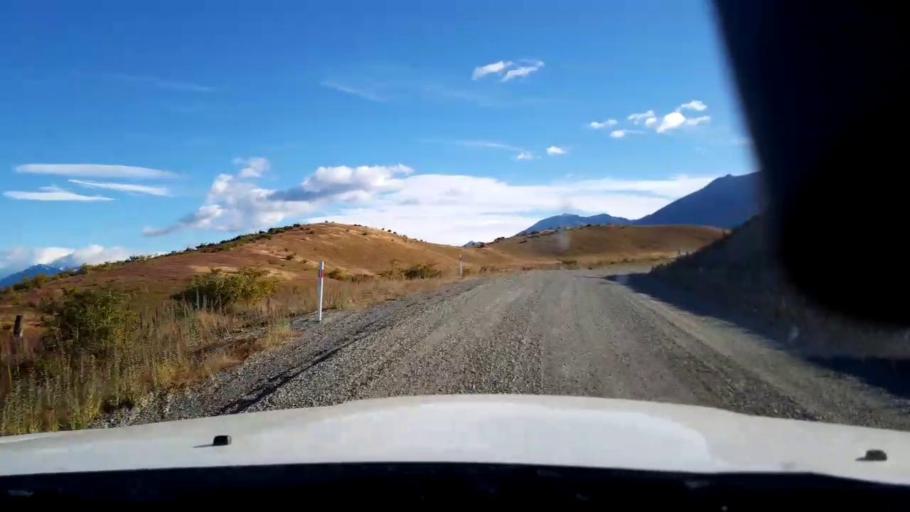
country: NZ
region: Canterbury
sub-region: Timaru District
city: Pleasant Point
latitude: -43.9673
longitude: 170.5171
